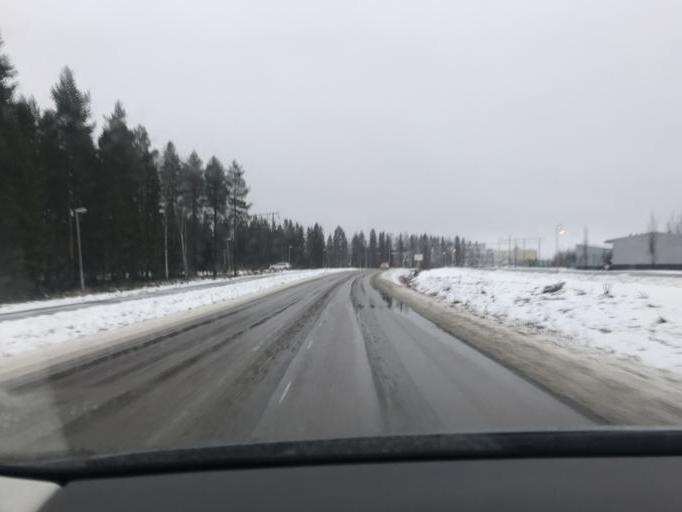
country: SE
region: Norrbotten
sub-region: Lulea Kommun
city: Bergnaset
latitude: 65.6137
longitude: 22.1195
